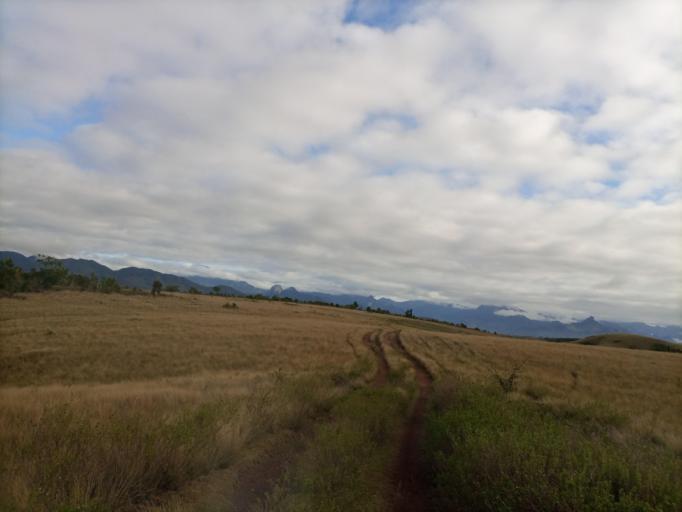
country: MG
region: Anosy
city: Fort Dauphin
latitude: -24.3123
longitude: 47.2515
